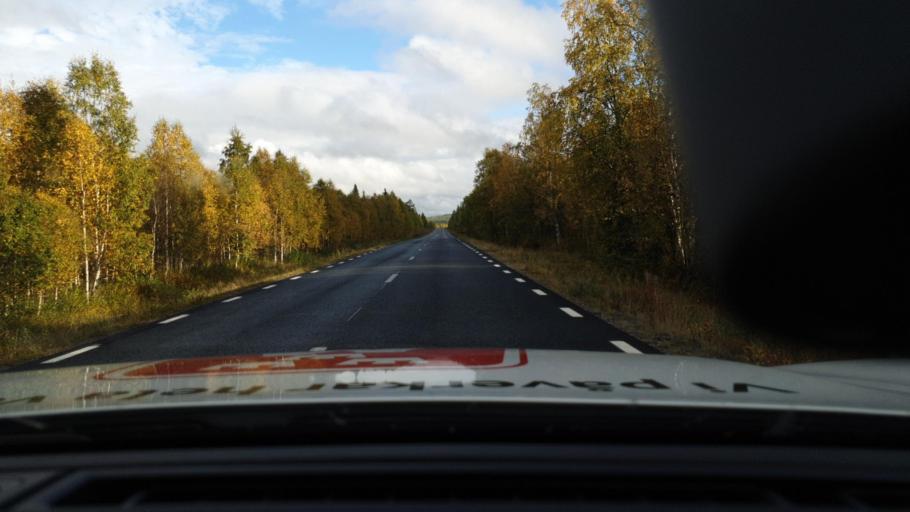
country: SE
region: Norrbotten
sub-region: Overkalix Kommun
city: OEverkalix
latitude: 66.9205
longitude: 22.7503
